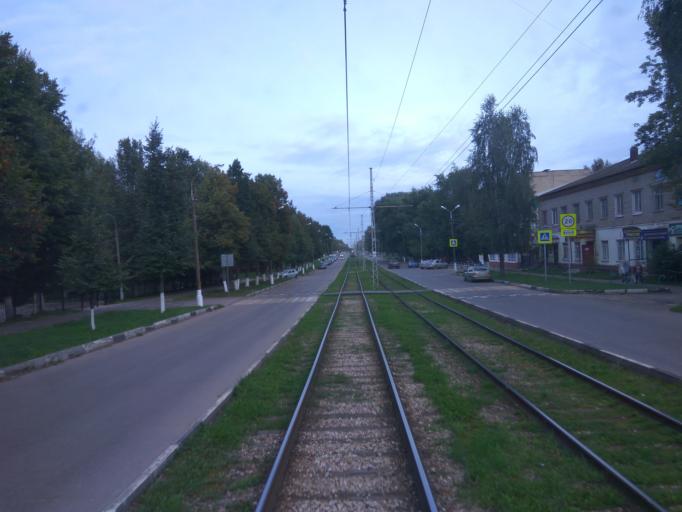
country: RU
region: Moskovskaya
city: Kolomna
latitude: 55.0802
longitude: 38.7644
